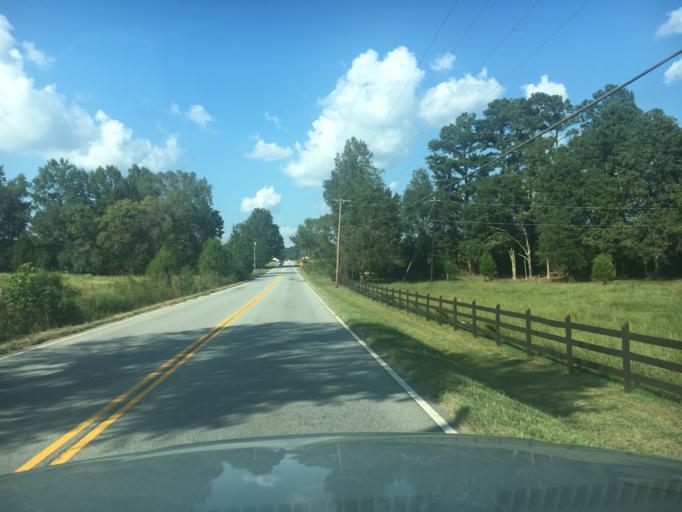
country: US
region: South Carolina
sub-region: Greenville County
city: Fountain Inn
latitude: 34.6689
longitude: -82.2603
